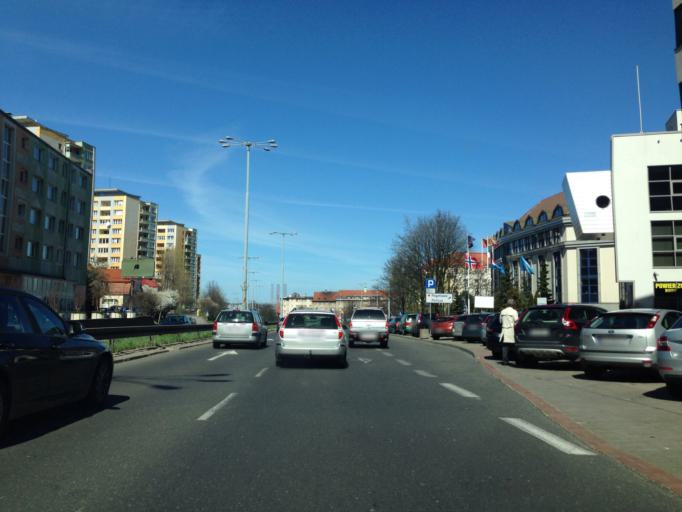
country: PL
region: Pomeranian Voivodeship
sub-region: Gdynia
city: Gdynia
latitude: 54.5160
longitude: 18.5321
